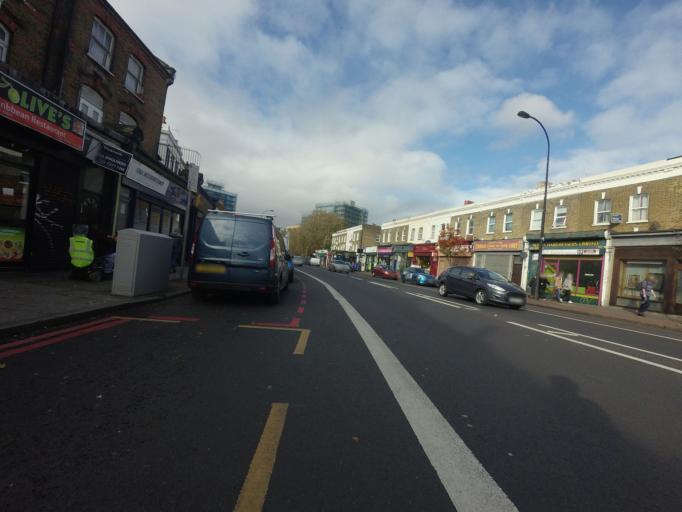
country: GB
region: England
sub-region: Greater London
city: Catford
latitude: 51.4758
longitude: -0.0474
